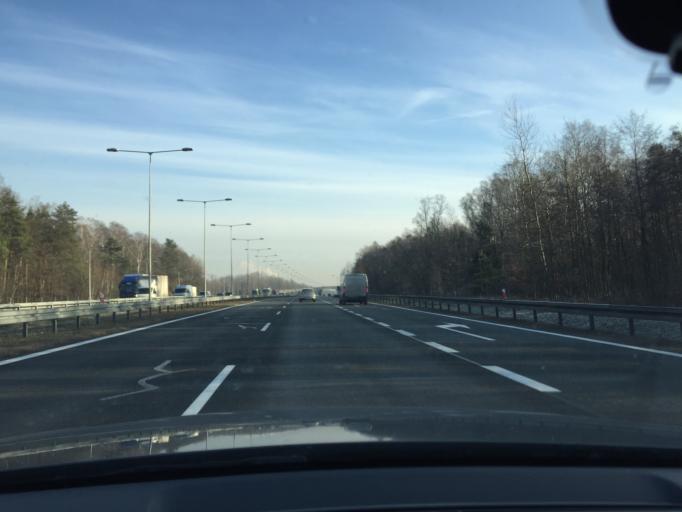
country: PL
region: Silesian Voivodeship
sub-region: Myslowice
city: Myslowice
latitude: 50.2176
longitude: 19.1204
